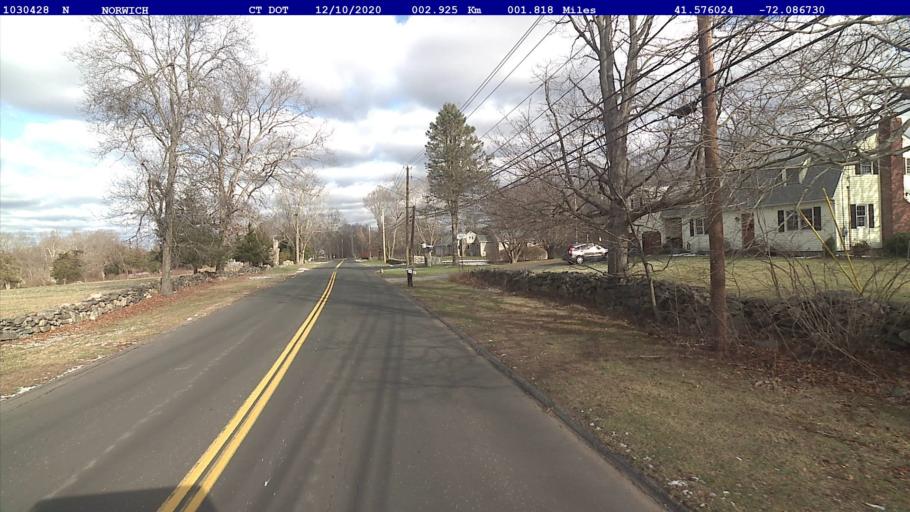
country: US
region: Connecticut
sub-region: New London County
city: Baltic
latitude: 41.5760
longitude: -72.0867
